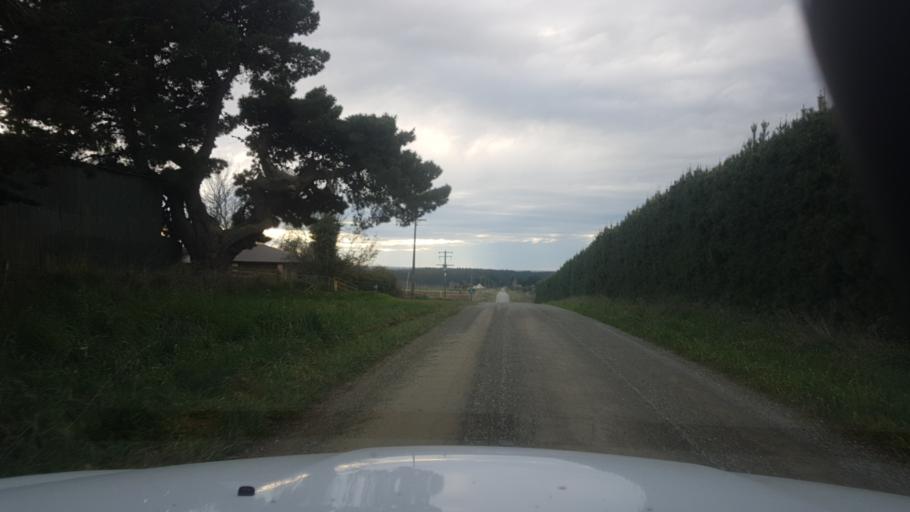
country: NZ
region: Canterbury
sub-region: Timaru District
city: Pleasant Point
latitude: -44.3378
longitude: 171.1480
